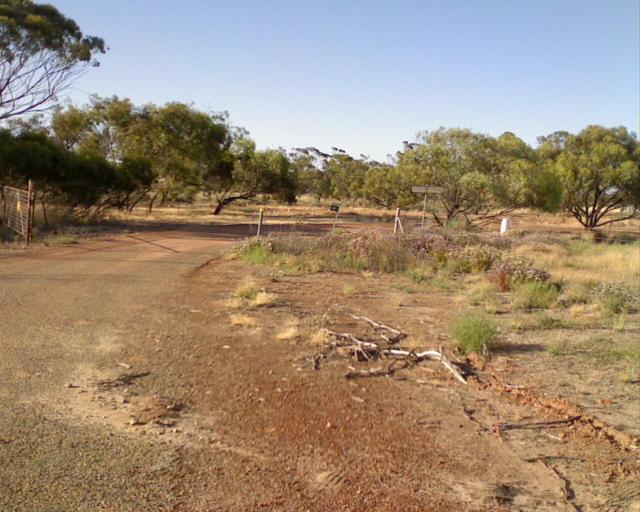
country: AU
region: Western Australia
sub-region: Moora
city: Moora
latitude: -30.2953
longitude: 116.0563
